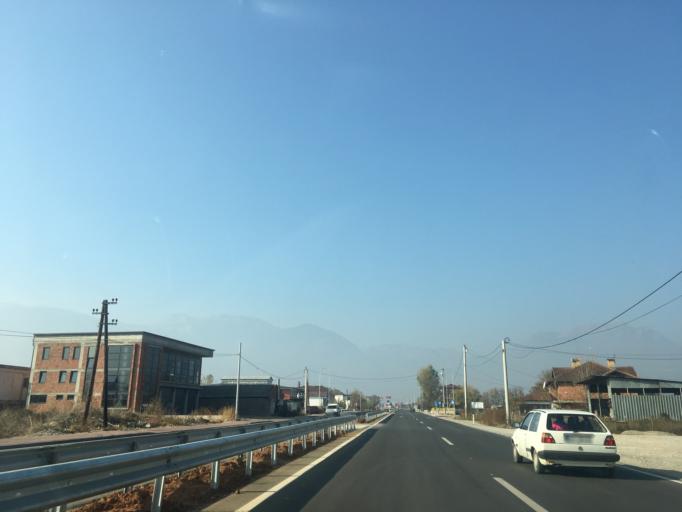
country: XK
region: Pec
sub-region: Komuna e Pejes
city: Dubova (Driloni)
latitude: 42.6584
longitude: 20.3519
